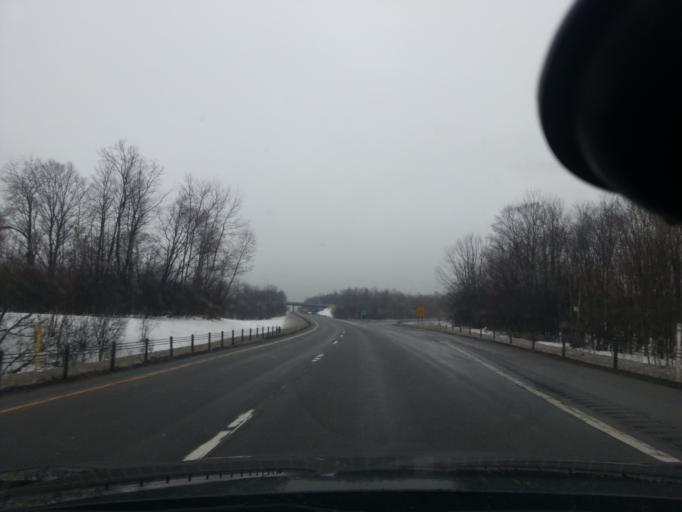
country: US
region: New York
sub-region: Jefferson County
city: Adams
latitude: 43.7413
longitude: -76.0736
